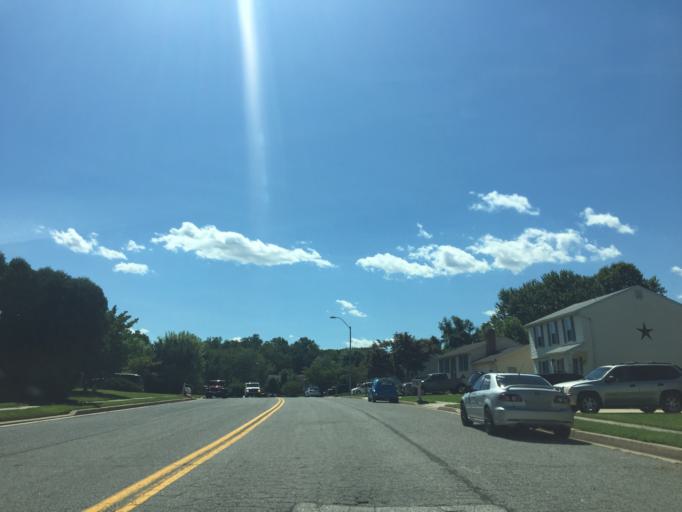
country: US
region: Maryland
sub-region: Baltimore County
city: Perry Hall
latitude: 39.4103
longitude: -76.4879
